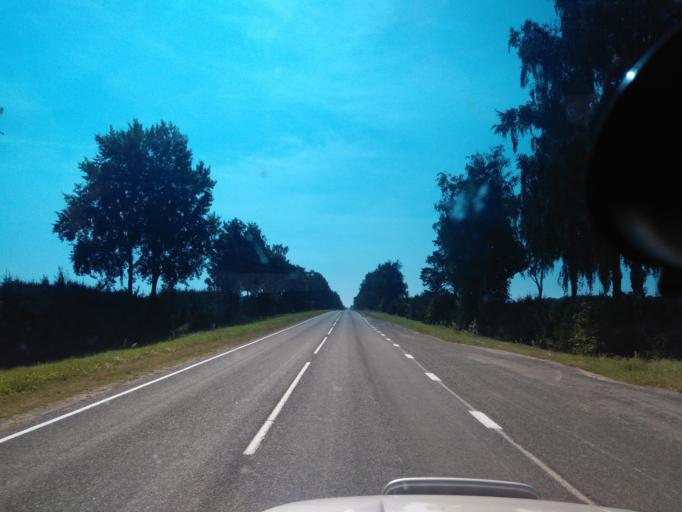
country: BY
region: Minsk
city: Uzda
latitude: 53.3507
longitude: 27.2263
